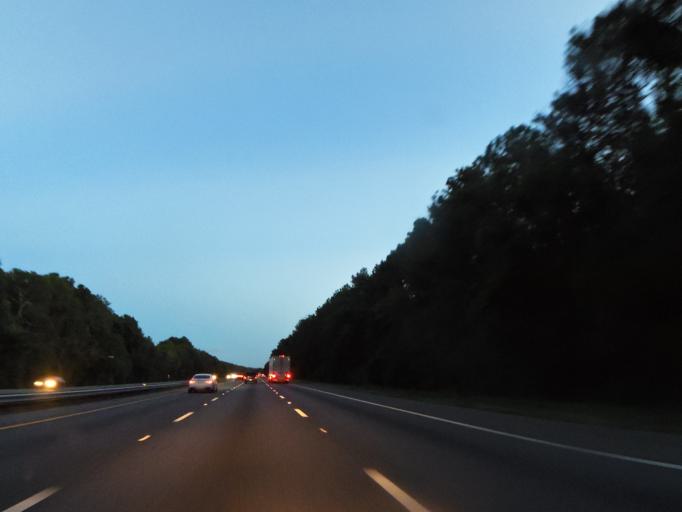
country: US
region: Florida
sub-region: Nassau County
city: Yulee
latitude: 30.5531
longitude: -81.6412
